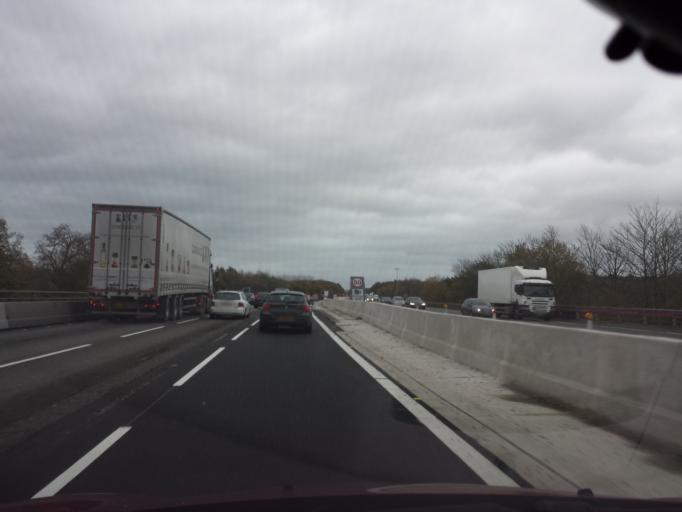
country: GB
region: England
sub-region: Surrey
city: Windlesham
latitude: 51.3671
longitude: -0.6340
